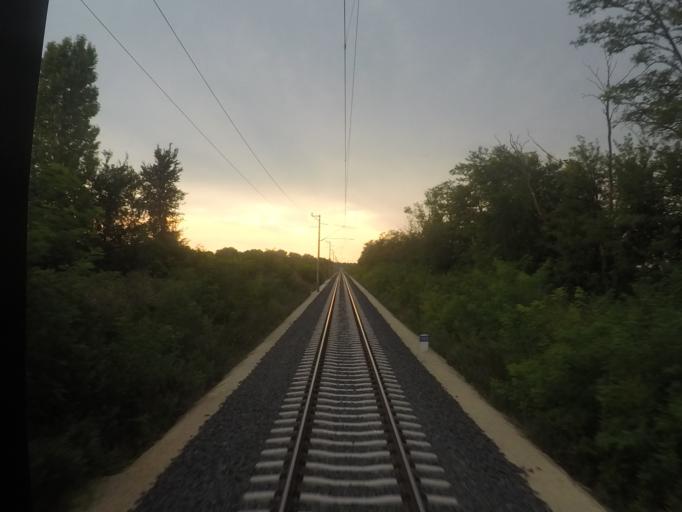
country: HU
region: Fejer
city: Lepseny
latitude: 46.9793
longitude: 18.2061
